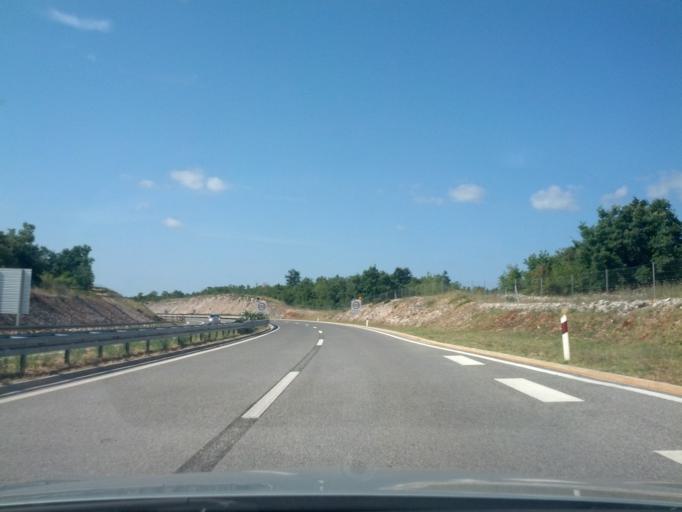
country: HR
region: Istarska
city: Buje
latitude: 45.4325
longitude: 13.6133
